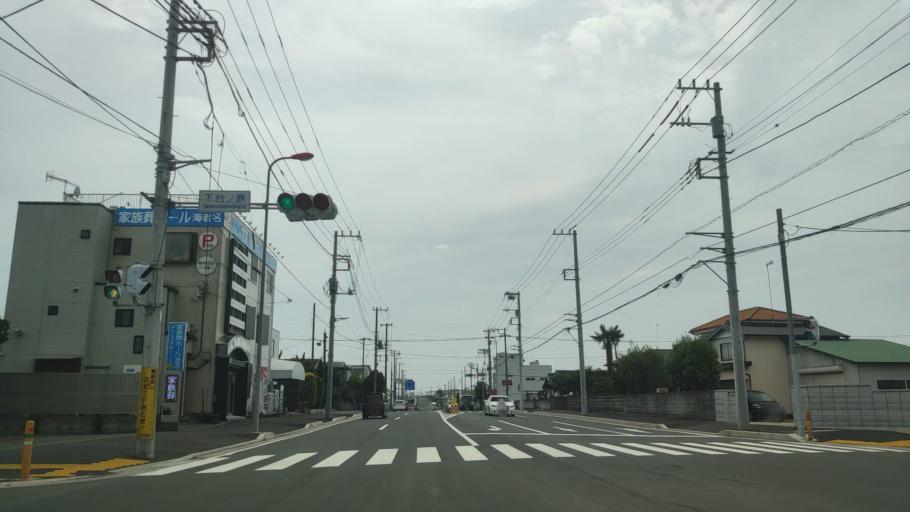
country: JP
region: Kanagawa
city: Atsugi
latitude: 35.4295
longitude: 139.3829
